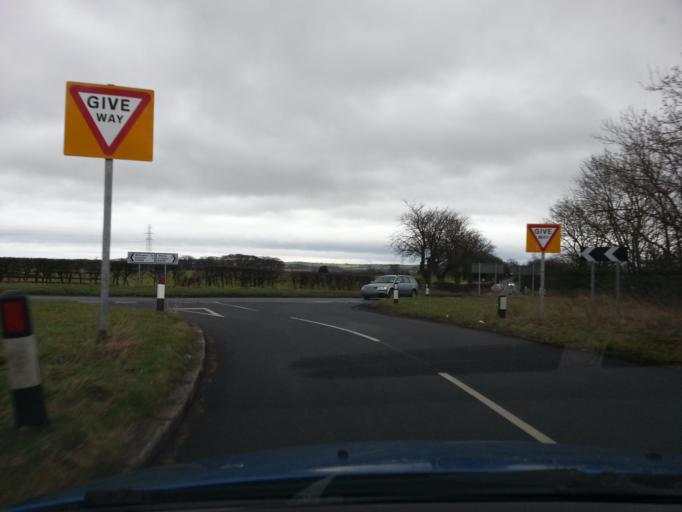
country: GB
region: England
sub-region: County Durham
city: Crook
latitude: 54.6827
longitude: -1.7178
